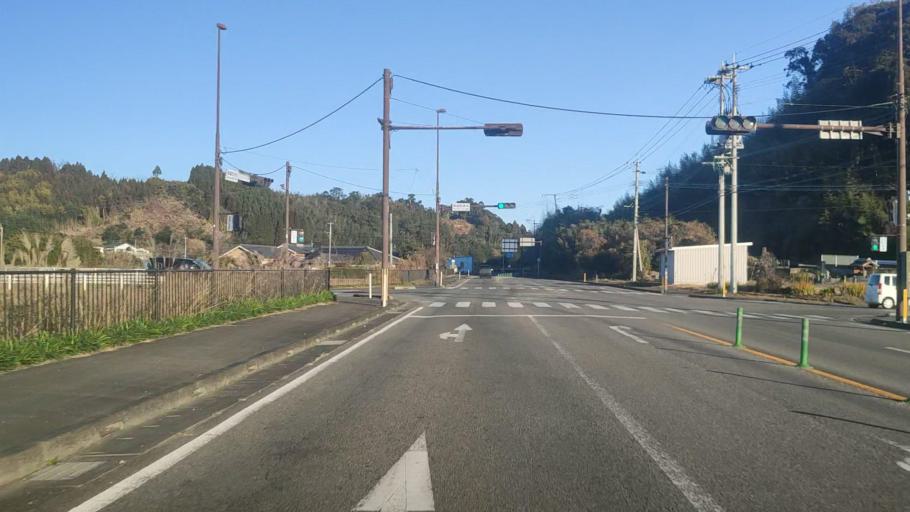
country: JP
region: Miyazaki
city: Takanabe
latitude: 32.1451
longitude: 131.5261
